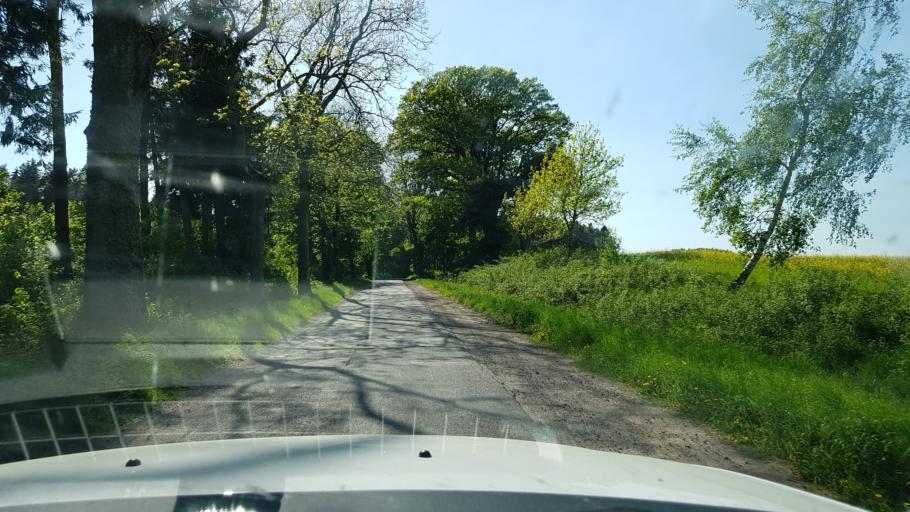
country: PL
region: West Pomeranian Voivodeship
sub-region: Powiat kolobrzeski
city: Ryman
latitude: 53.9939
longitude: 15.5294
